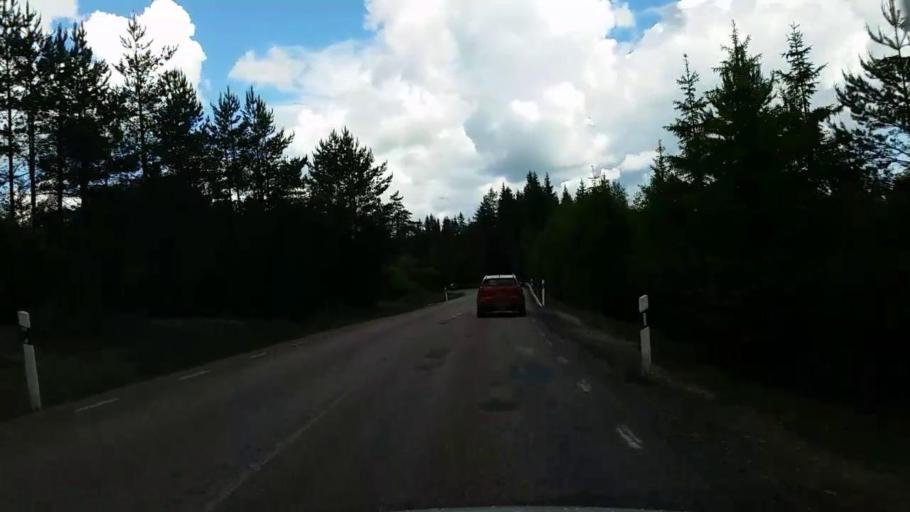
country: SE
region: Vaestmanland
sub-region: Fagersta Kommun
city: Fagersta
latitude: 59.8797
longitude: 15.8367
